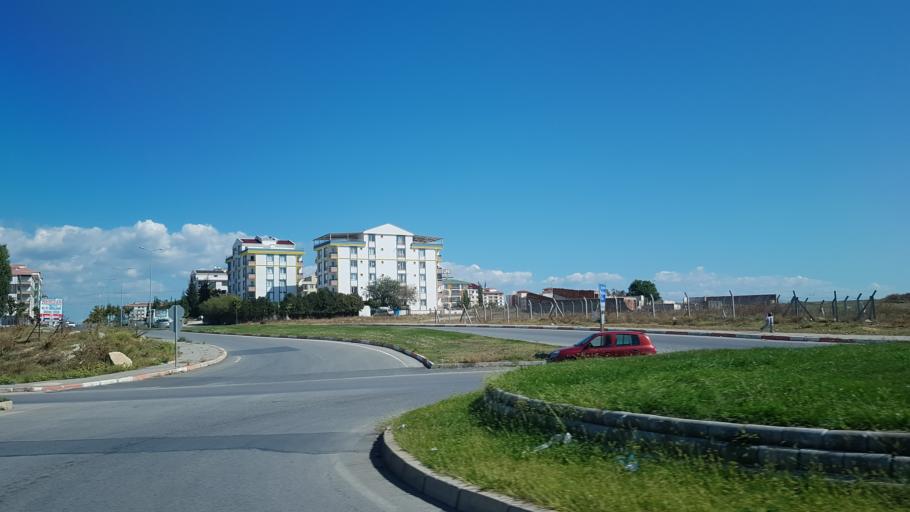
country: TR
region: Kirklareli
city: Kirklareli
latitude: 41.7509
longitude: 27.2190
